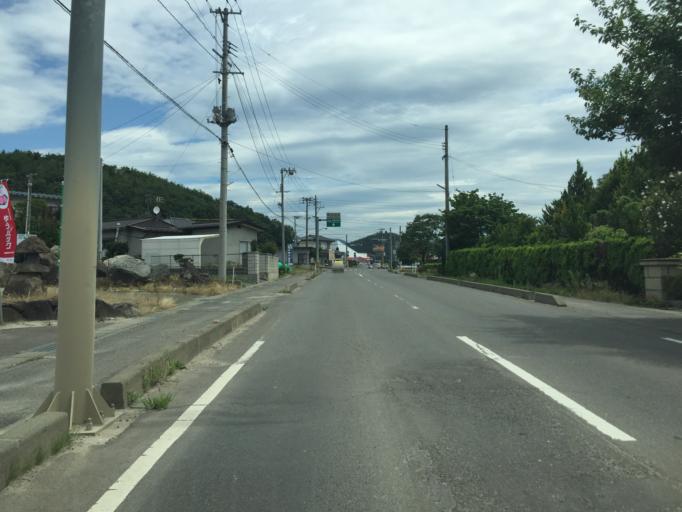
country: JP
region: Fukushima
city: Fukushima-shi
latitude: 37.8098
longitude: 140.4163
